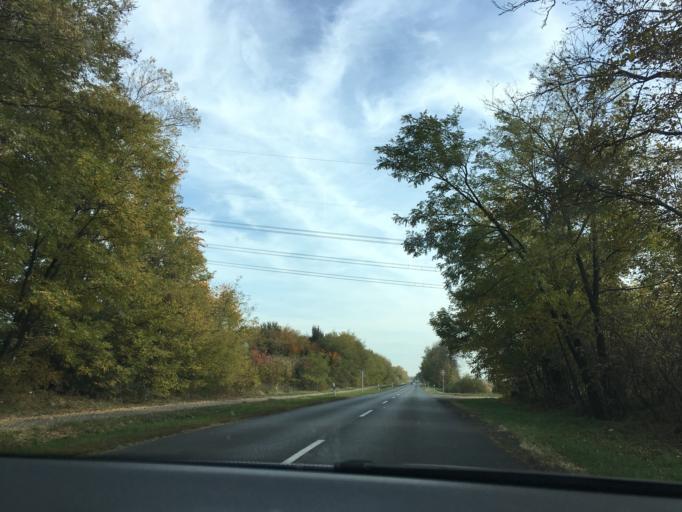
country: HU
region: Szabolcs-Szatmar-Bereg
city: Nagykallo
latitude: 47.8641
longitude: 21.8855
